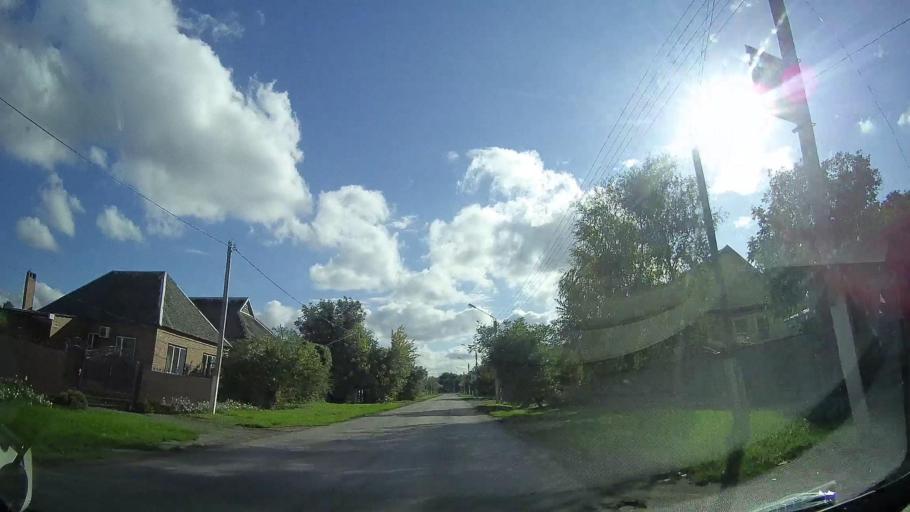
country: RU
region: Rostov
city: Tselina
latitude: 46.5323
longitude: 41.0335
